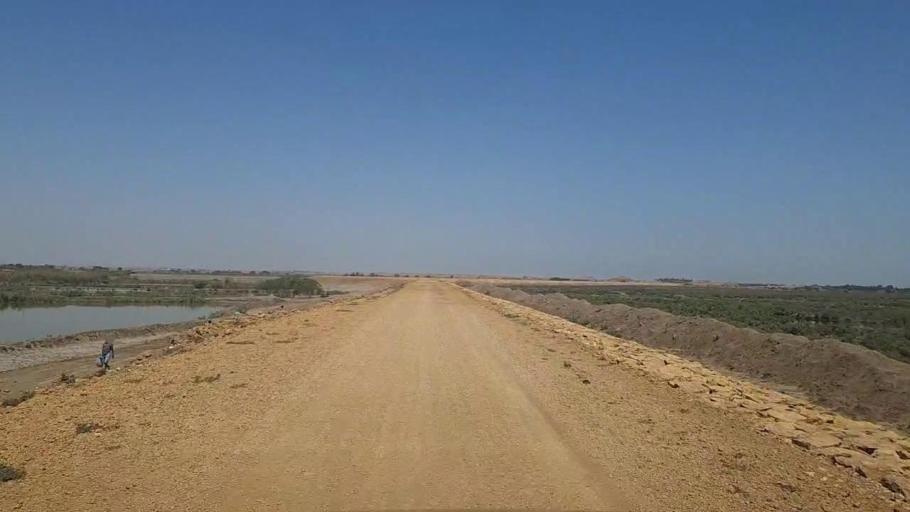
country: PK
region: Sindh
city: Thatta
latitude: 24.7967
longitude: 67.9987
